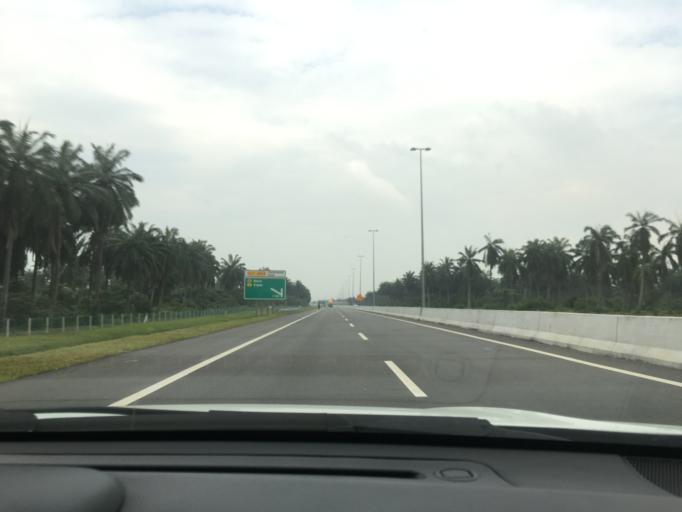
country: MY
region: Selangor
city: Klang
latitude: 3.1187
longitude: 101.4094
